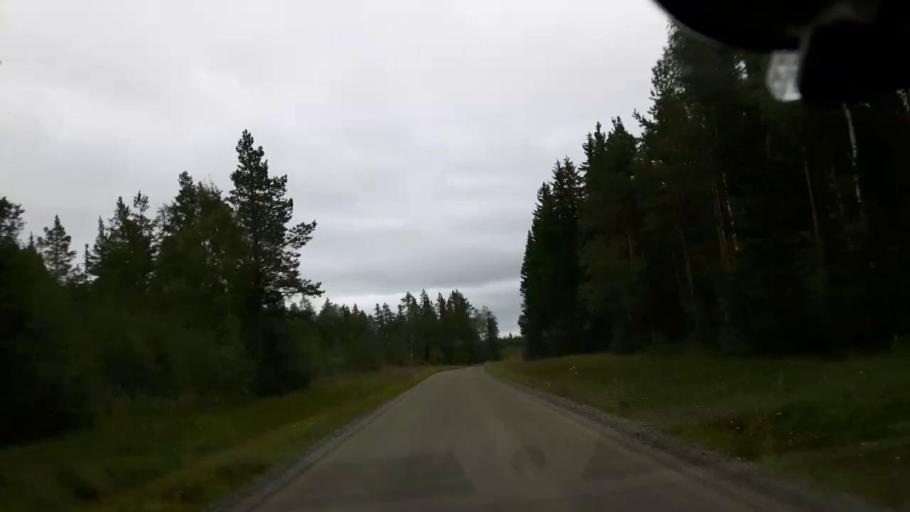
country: SE
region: Vaesternorrland
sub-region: Ange Kommun
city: Fransta
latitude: 62.7766
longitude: 15.9553
